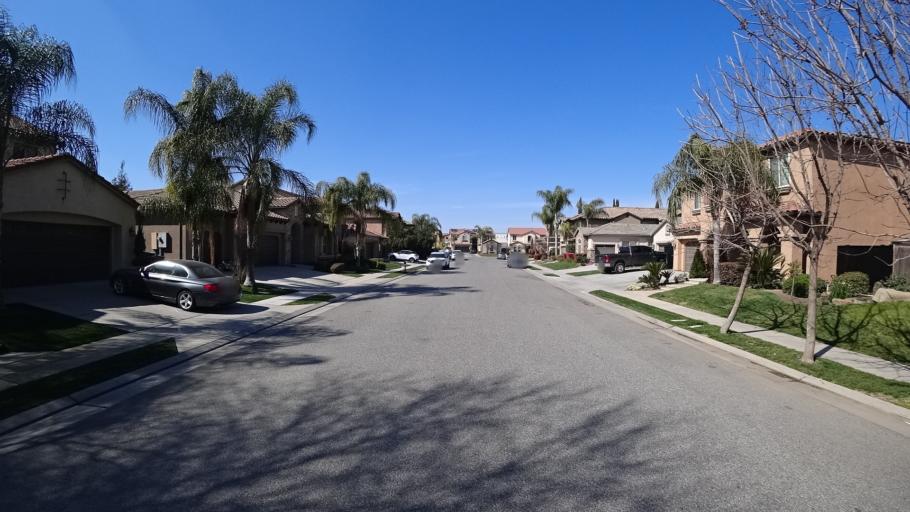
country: US
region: California
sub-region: Fresno County
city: Clovis
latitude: 36.8976
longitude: -119.7607
